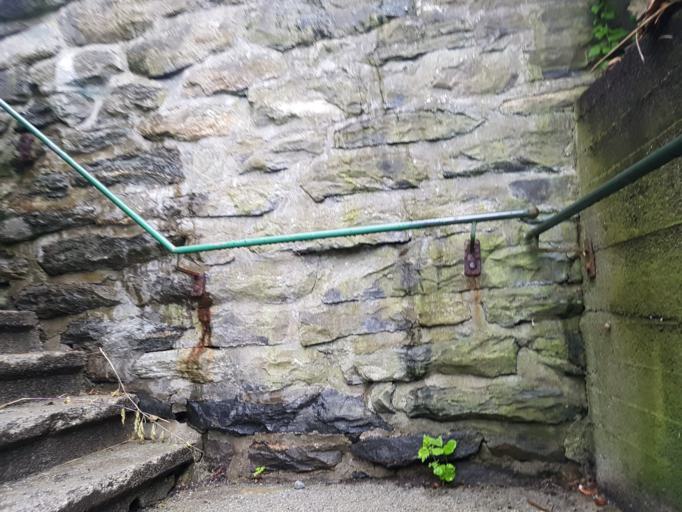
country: NO
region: Hordaland
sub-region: Bergen
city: Bergen
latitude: 60.3982
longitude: 5.3307
